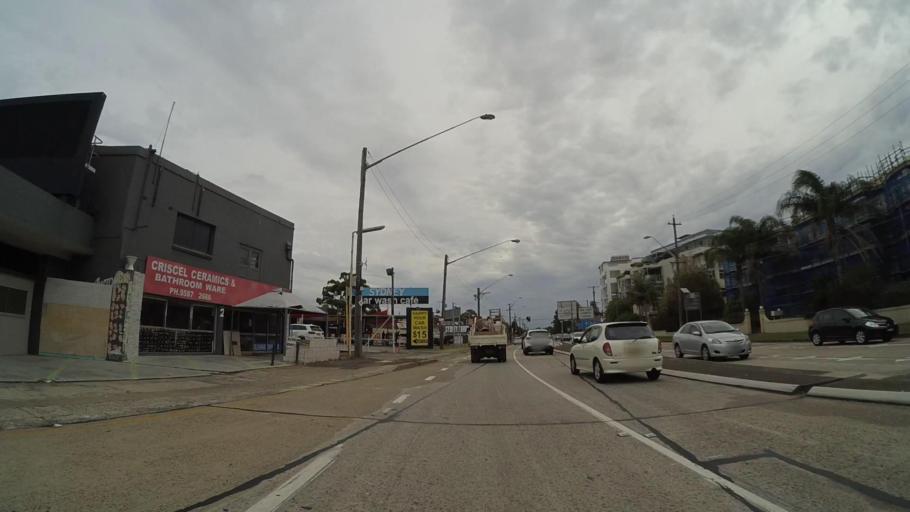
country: AU
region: New South Wales
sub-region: Kogarah
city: Beverly Park
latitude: -33.9693
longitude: 151.1359
